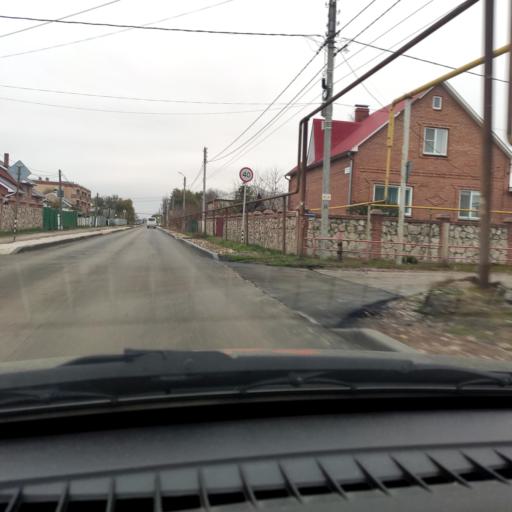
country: RU
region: Samara
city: Podstepki
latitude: 53.5108
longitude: 49.2378
